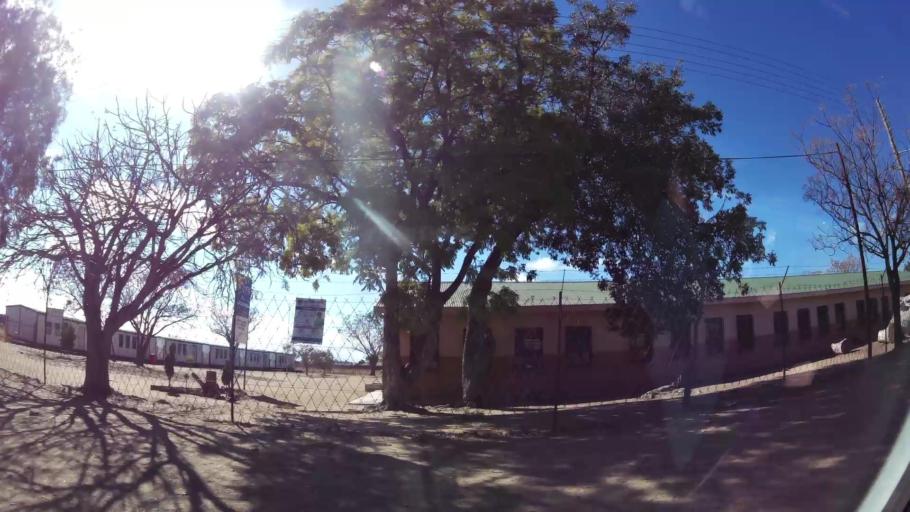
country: ZA
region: Limpopo
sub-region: Capricorn District Municipality
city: Polokwane
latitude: -23.8629
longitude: 29.3884
